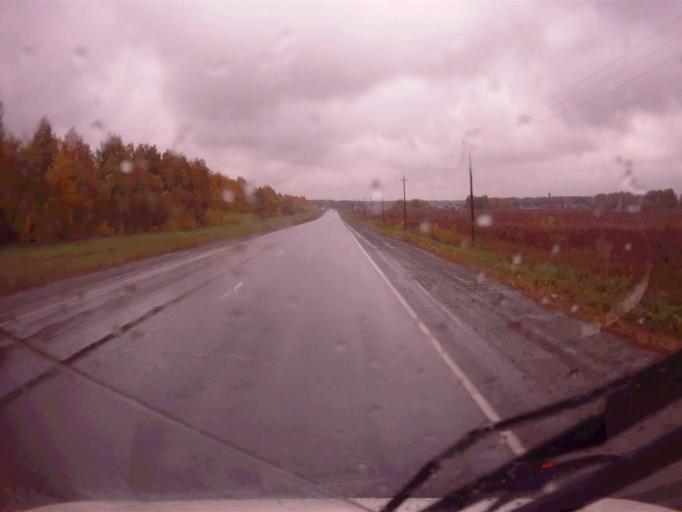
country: RU
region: Chelyabinsk
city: Argayash
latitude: 55.4031
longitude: 61.0668
